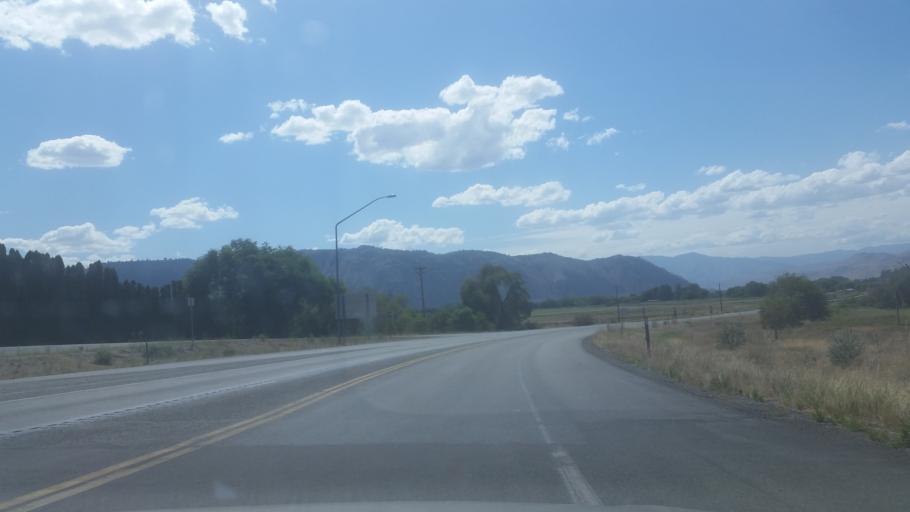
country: US
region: Washington
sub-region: Okanogan County
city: Brewster
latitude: 48.1040
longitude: -119.6854
